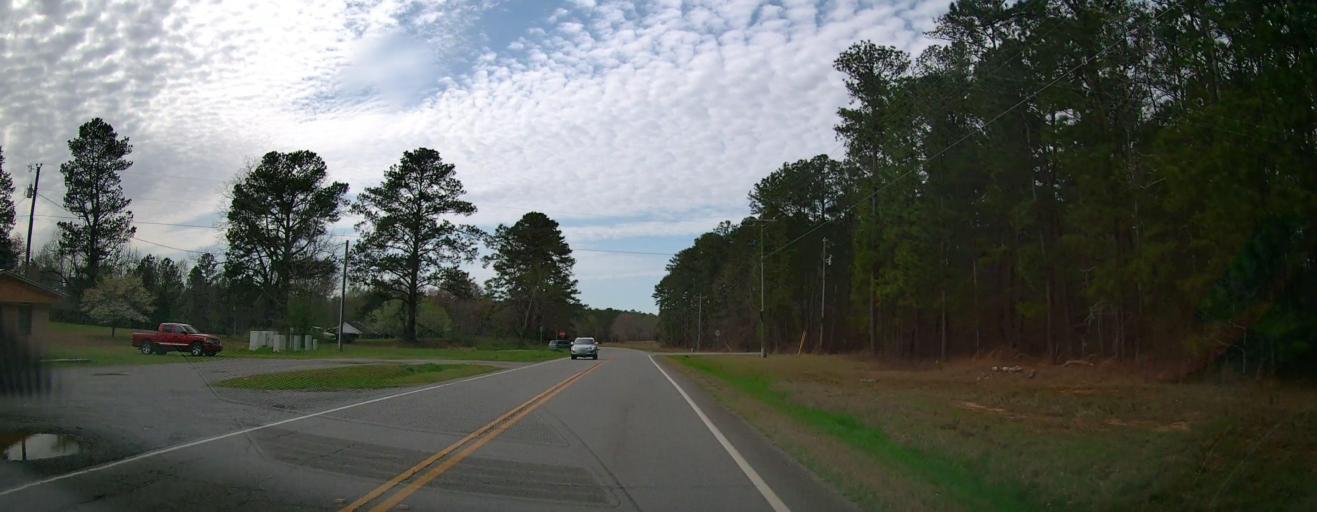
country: US
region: Georgia
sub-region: Jones County
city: Gray
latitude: 32.9826
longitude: -83.6647
